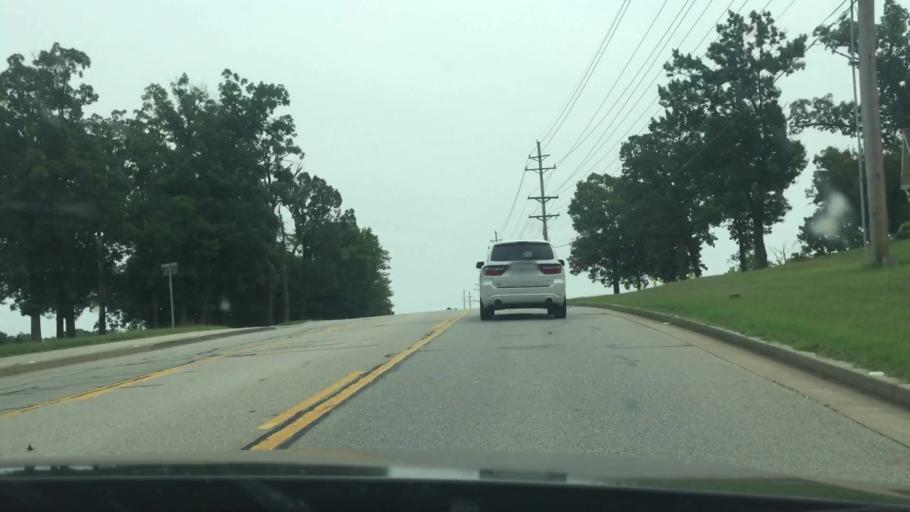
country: US
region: Missouri
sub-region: Camden County
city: Four Seasons
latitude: 38.1910
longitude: -92.6844
